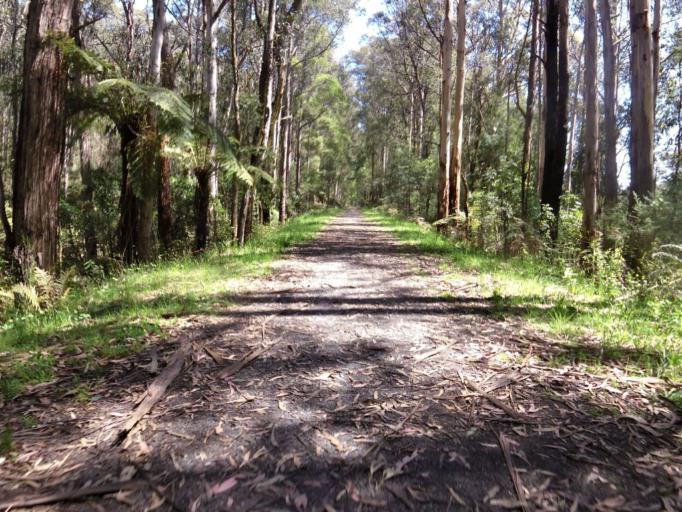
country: AU
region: Victoria
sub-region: Baw Baw
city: Warragul
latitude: -37.8960
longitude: 145.9918
